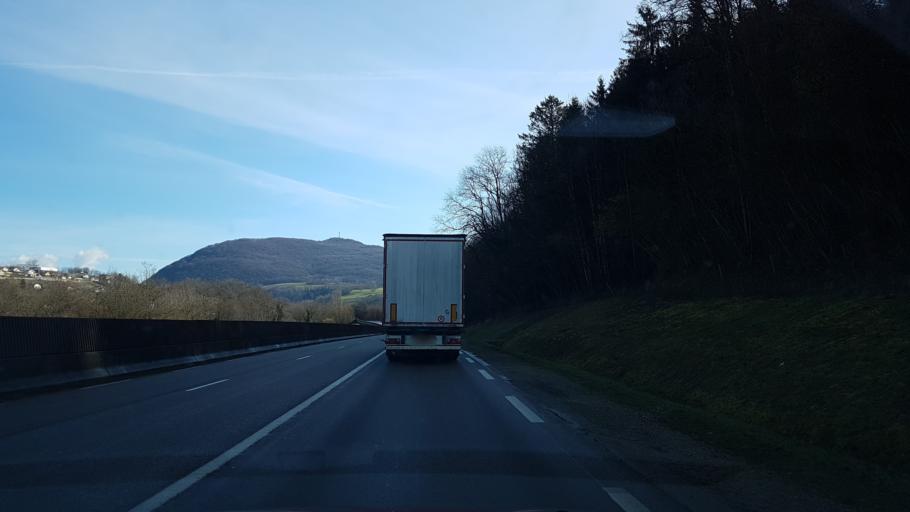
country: FR
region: Rhone-Alpes
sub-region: Departement de la Haute-Savoie
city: Frangy
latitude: 46.0163
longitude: 5.9276
